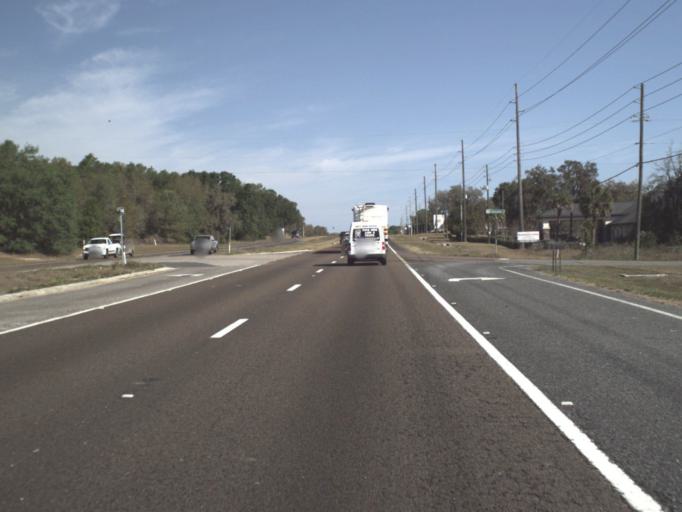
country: US
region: Florida
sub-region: Lake County
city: Hawthorne
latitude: 28.7544
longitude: -81.8782
